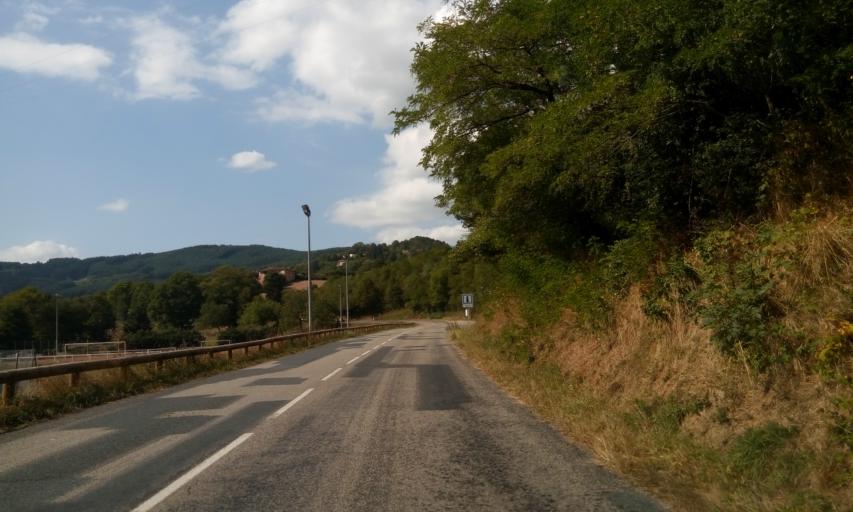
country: FR
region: Rhone-Alpes
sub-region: Departement du Rhone
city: Grandris
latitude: 46.0046
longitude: 4.4593
